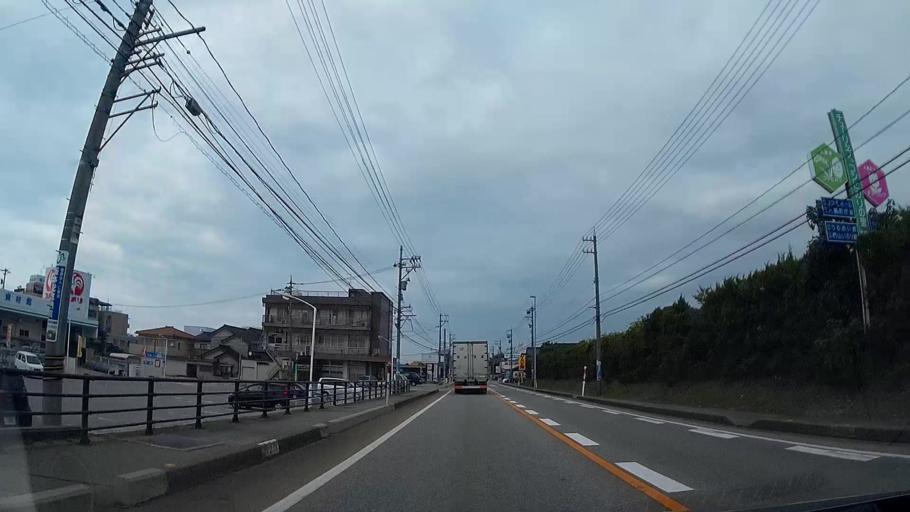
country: JP
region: Toyama
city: Nyuzen
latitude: 36.9316
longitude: 137.5010
